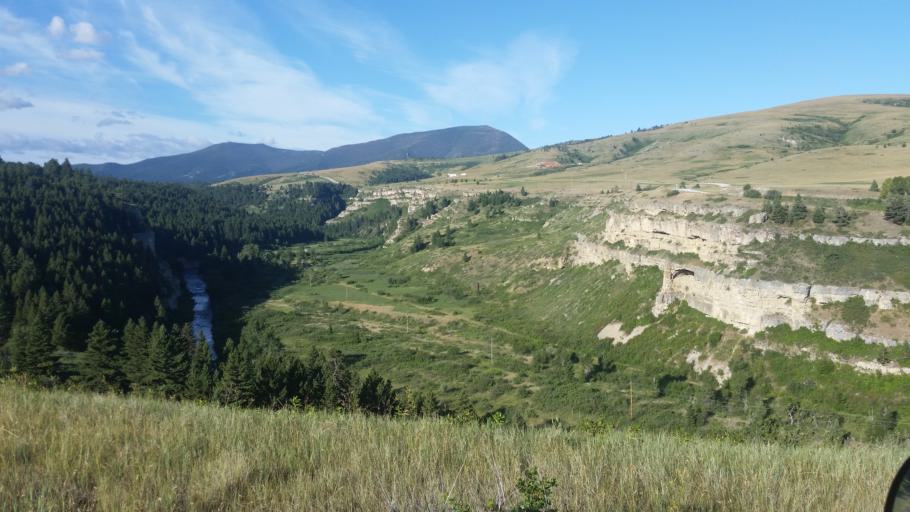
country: US
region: Montana
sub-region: Cascade County
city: Malmstrom Air Force Base
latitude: 47.2107
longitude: -110.9304
